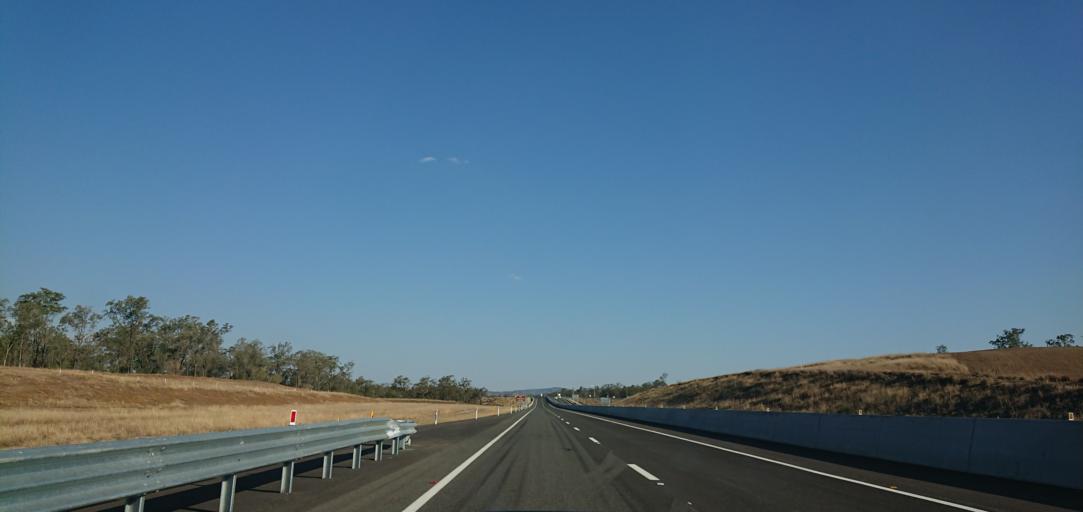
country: AU
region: Queensland
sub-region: Toowoomba
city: Rangeville
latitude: -27.5368
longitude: 152.0765
